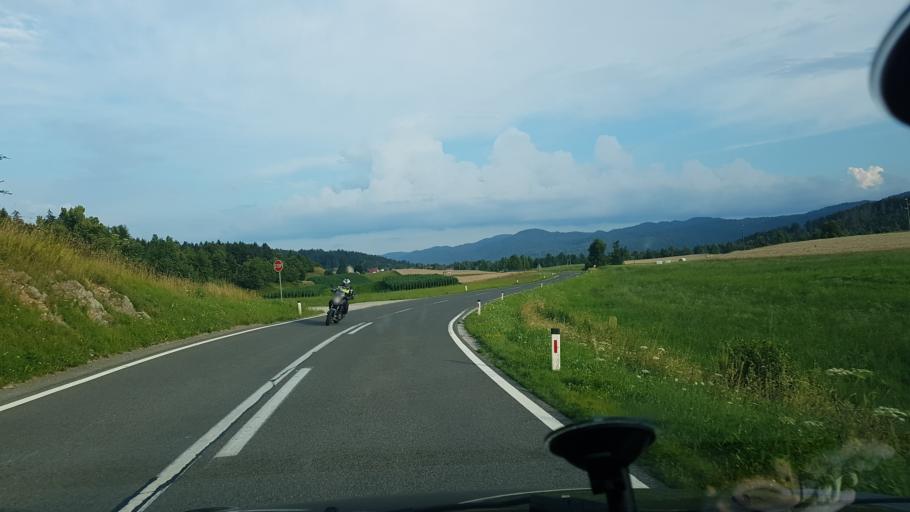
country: SI
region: Logatec
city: Logatec
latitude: 45.9368
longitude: 14.1292
